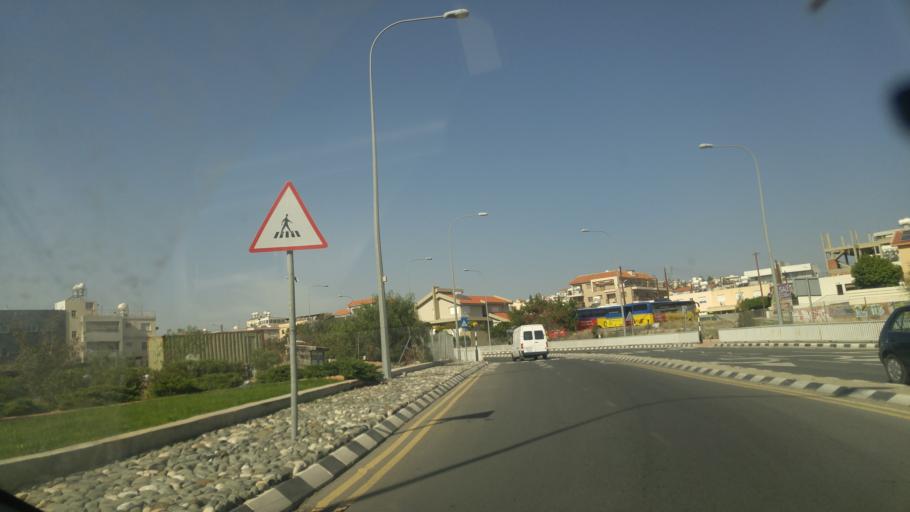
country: CY
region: Limassol
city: Limassol
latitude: 34.7059
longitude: 33.0460
